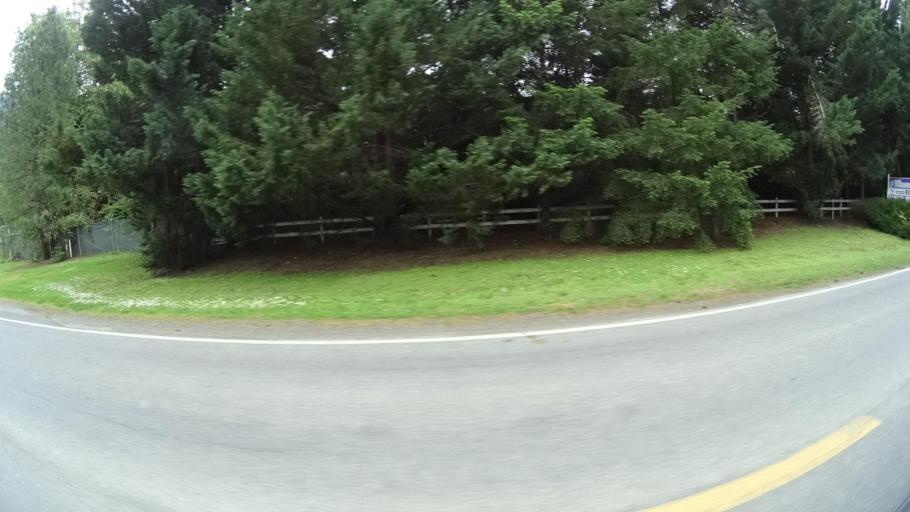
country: US
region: California
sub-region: Humboldt County
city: Willow Creek
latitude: 41.3000
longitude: -123.5467
